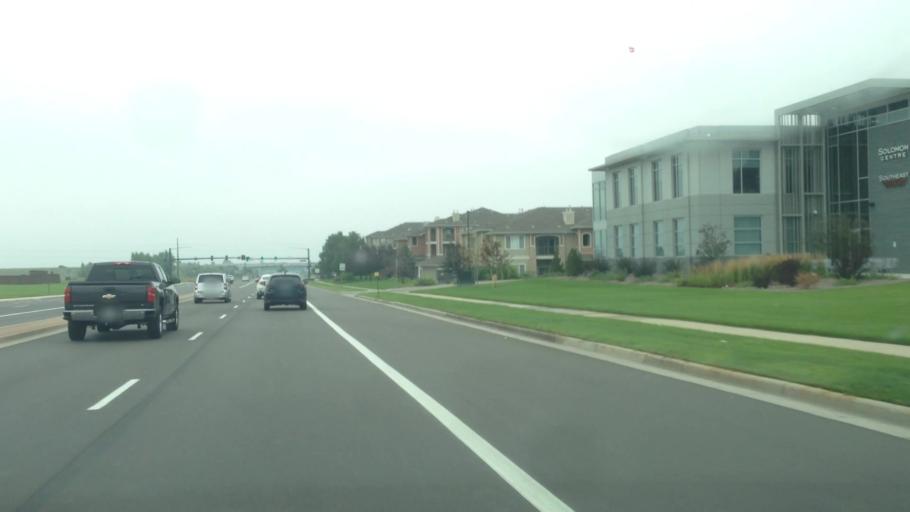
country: US
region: Colorado
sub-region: Douglas County
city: Stonegate
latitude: 39.5433
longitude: -104.7926
